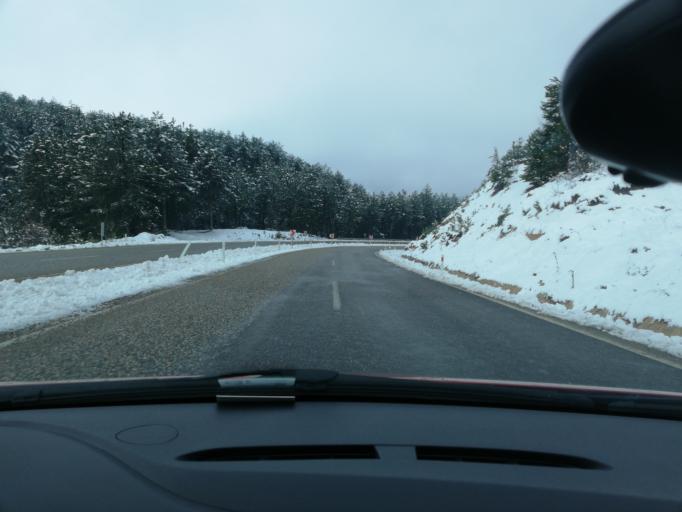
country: TR
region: Kastamonu
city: Akkaya
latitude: 41.2849
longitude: 33.4492
